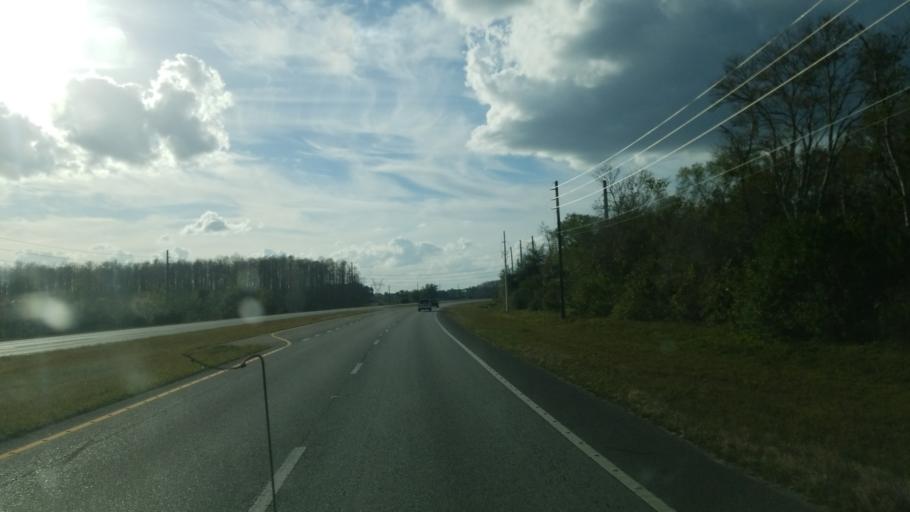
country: US
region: Florida
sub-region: Osceola County
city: Saint Cloud
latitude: 28.1448
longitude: -81.0842
